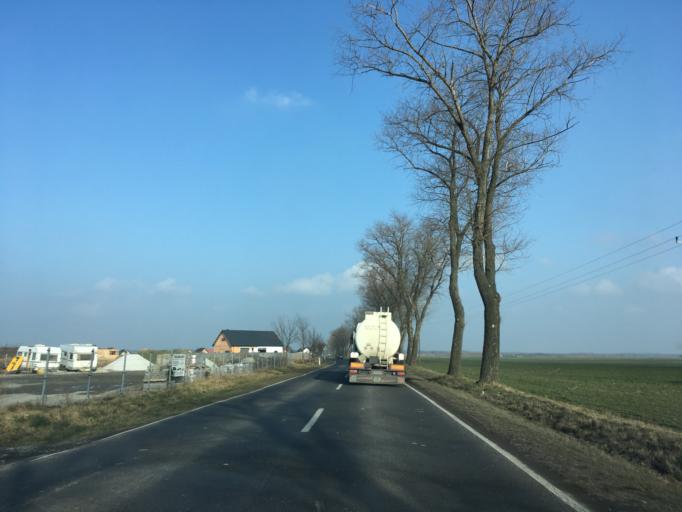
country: PL
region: Lower Silesian Voivodeship
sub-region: Powiat legnicki
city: Chojnow
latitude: 51.2837
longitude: 15.9497
